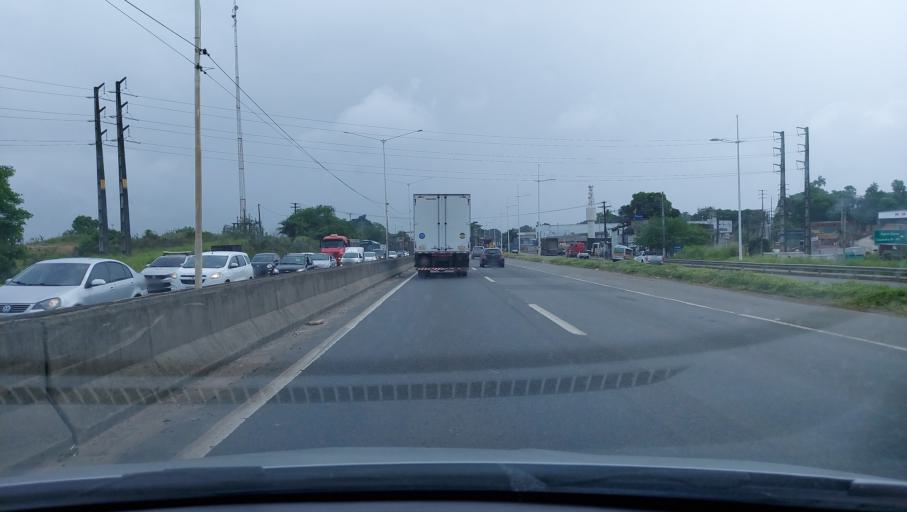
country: BR
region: Bahia
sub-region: Salvador
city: Salvador
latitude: -12.8888
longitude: -38.4424
